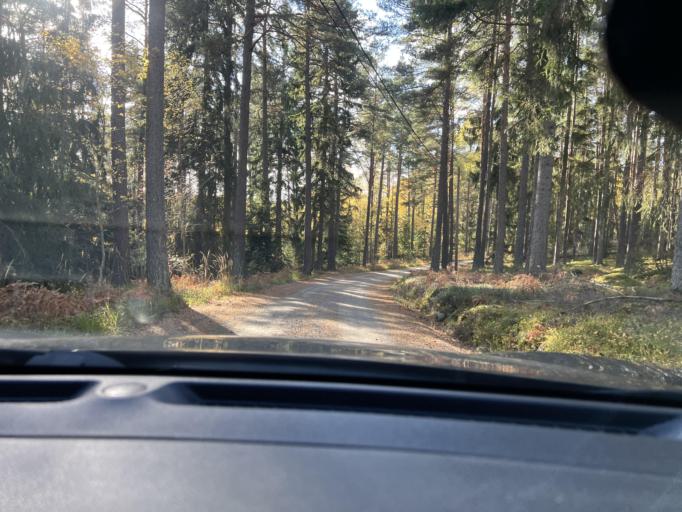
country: SE
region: Stockholm
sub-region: Vallentuna Kommun
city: Vallentuna
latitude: 59.5075
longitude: 18.1023
